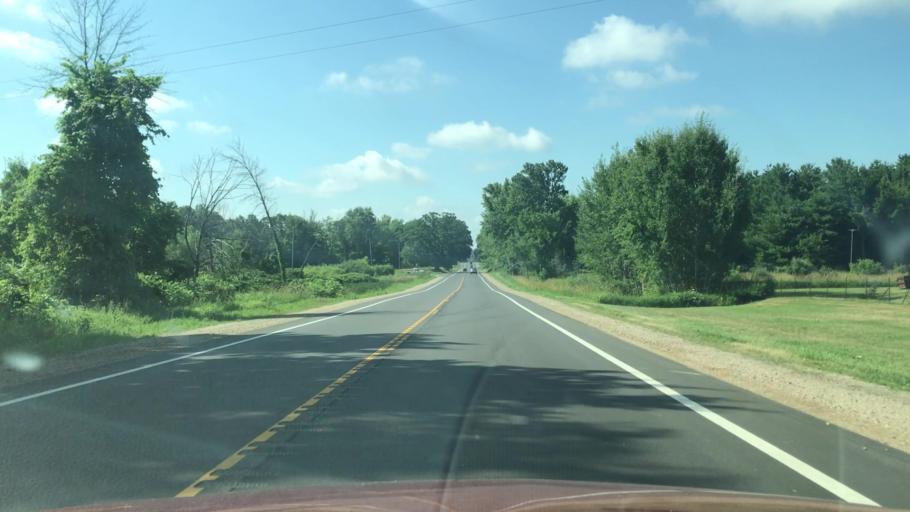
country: US
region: Michigan
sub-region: Newaygo County
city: Newaygo
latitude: 43.3797
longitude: -85.8009
